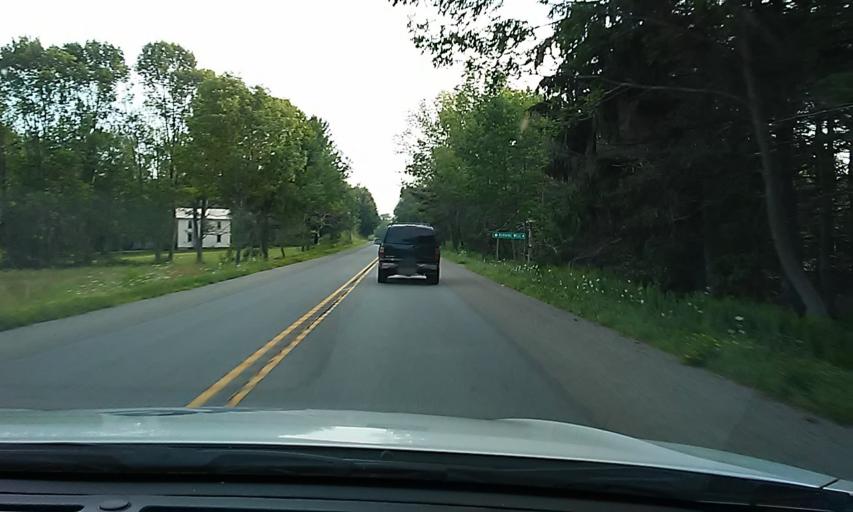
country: US
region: Pennsylvania
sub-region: McKean County
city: Kane
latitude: 41.6766
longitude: -78.7271
